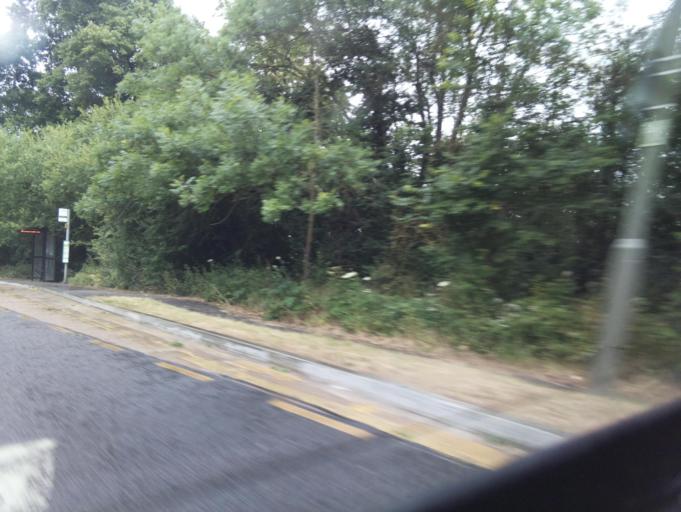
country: GB
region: England
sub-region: Surrey
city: Salfords
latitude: 51.2070
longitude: -0.1686
